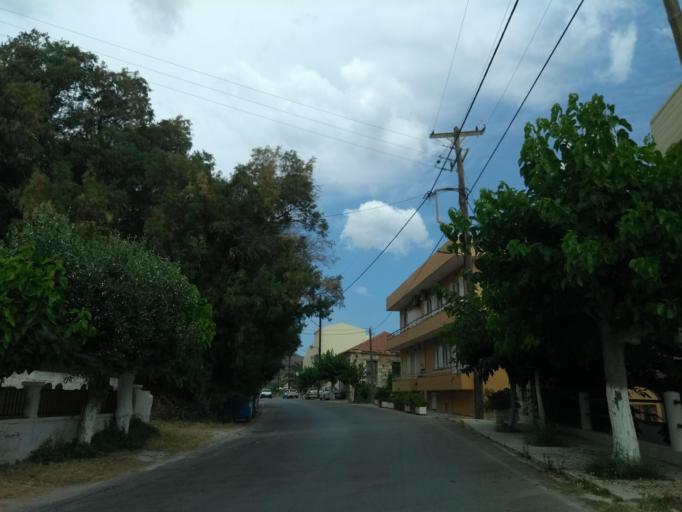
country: GR
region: Crete
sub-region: Nomos Chanias
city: Kalivai
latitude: 35.4573
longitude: 24.1674
